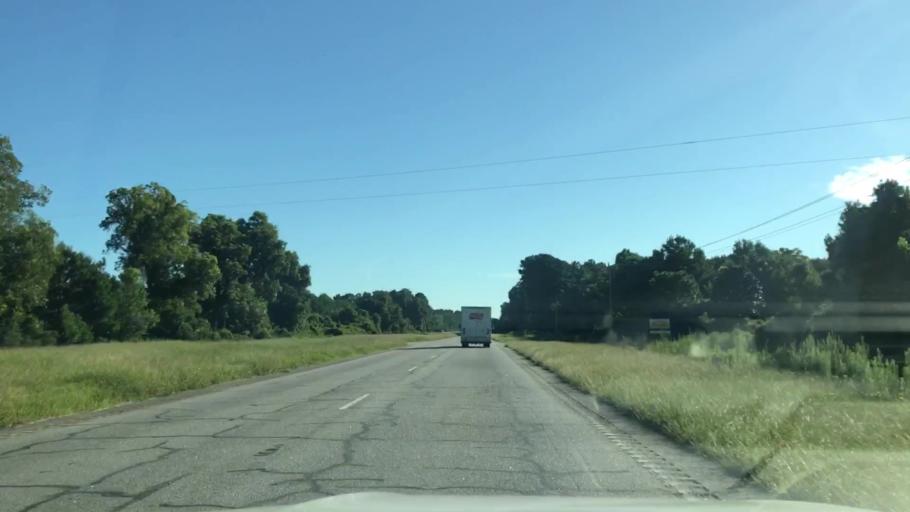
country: US
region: South Carolina
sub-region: Charleston County
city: Awendaw
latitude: 33.0568
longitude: -79.5442
